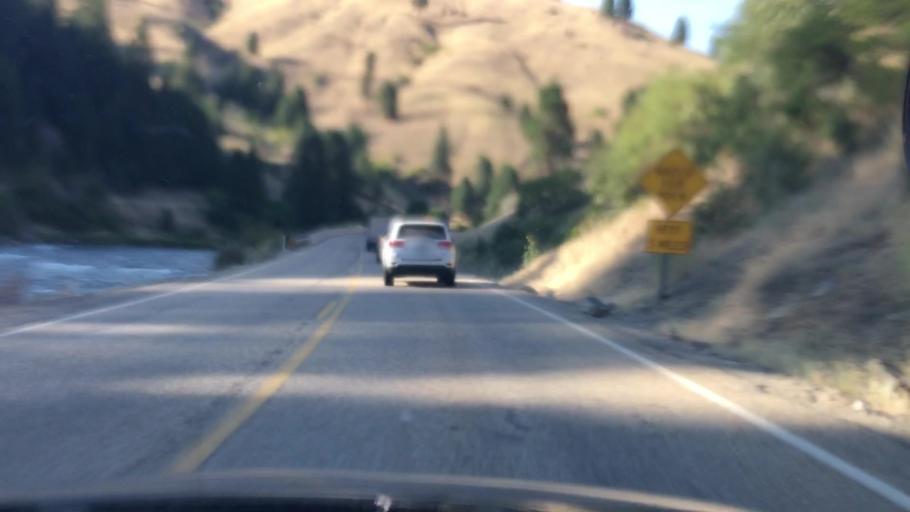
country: US
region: Idaho
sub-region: Boise County
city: Idaho City
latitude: 44.0978
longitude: -116.0993
